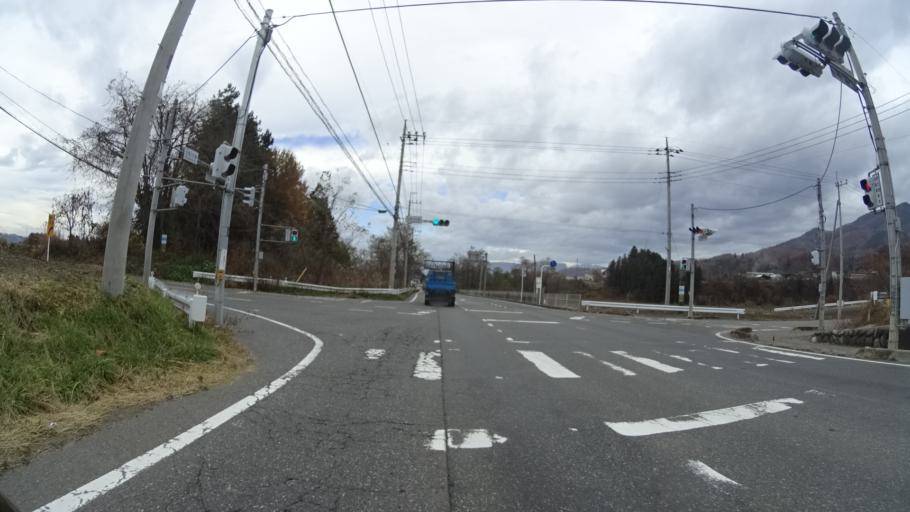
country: JP
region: Gunma
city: Numata
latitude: 36.6611
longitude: 139.1518
